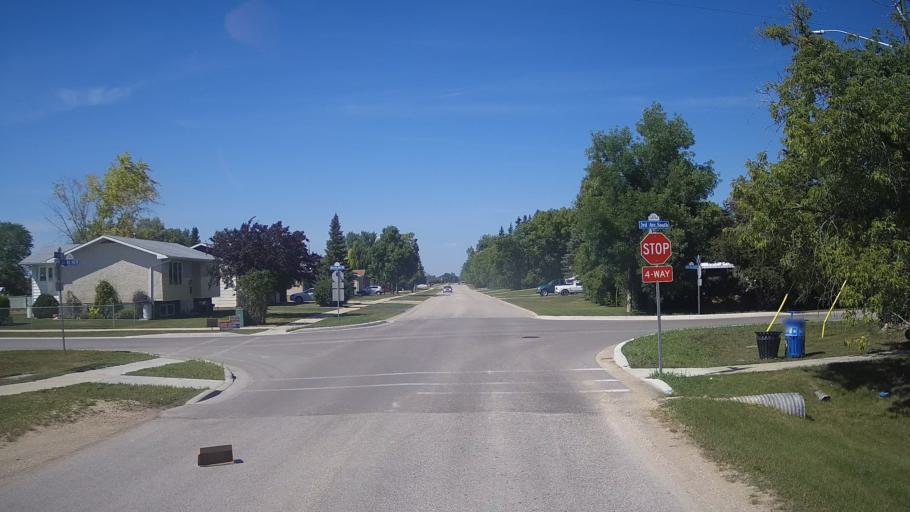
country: CA
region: Manitoba
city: Stonewall
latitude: 50.1299
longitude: -97.3338
